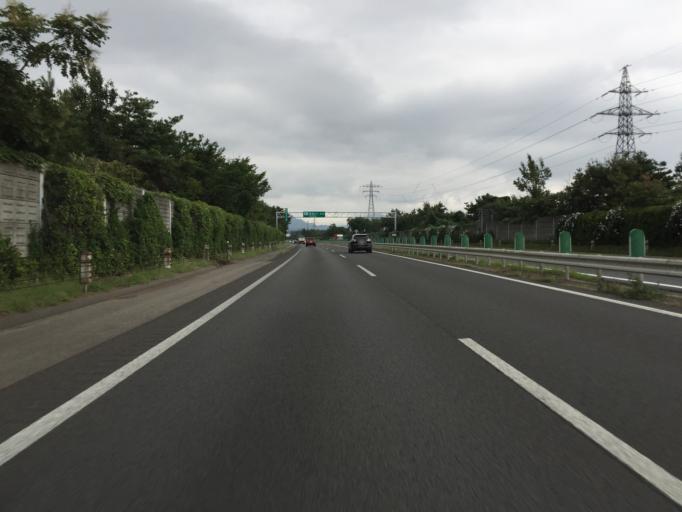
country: JP
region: Fukushima
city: Fukushima-shi
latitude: 37.7691
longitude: 140.4124
